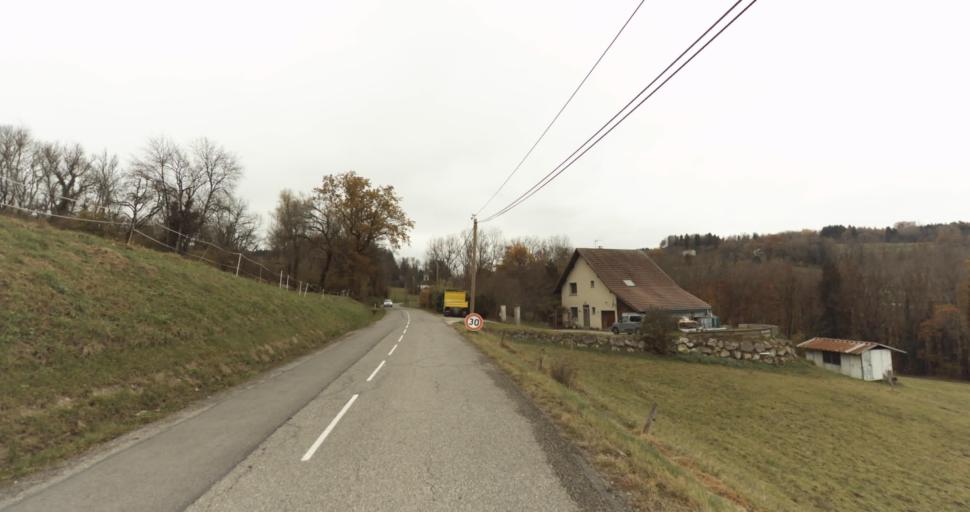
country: FR
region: Rhone-Alpes
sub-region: Departement de la Haute-Savoie
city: Thorens-Glieres
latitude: 45.9803
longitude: 6.2261
